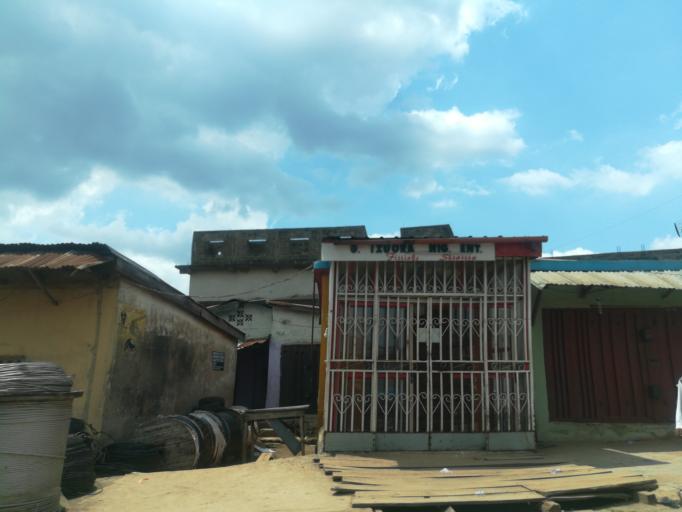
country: NG
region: Oyo
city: Ibadan
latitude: 7.3893
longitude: 3.8860
